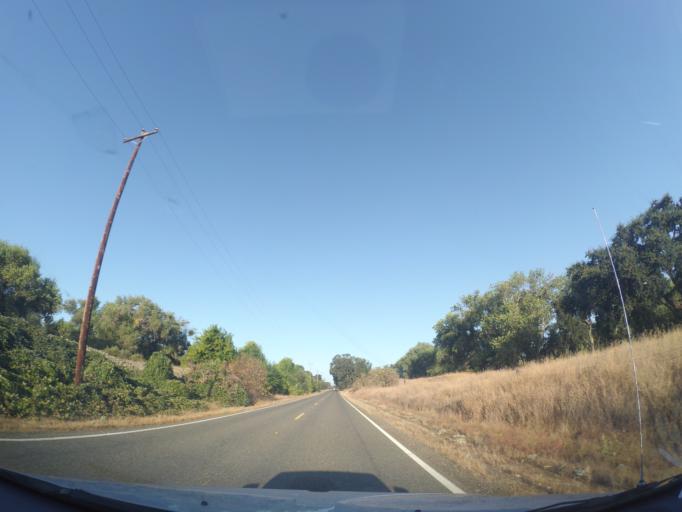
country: US
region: California
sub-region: Merced County
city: Planada
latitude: 37.5190
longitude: -120.3831
